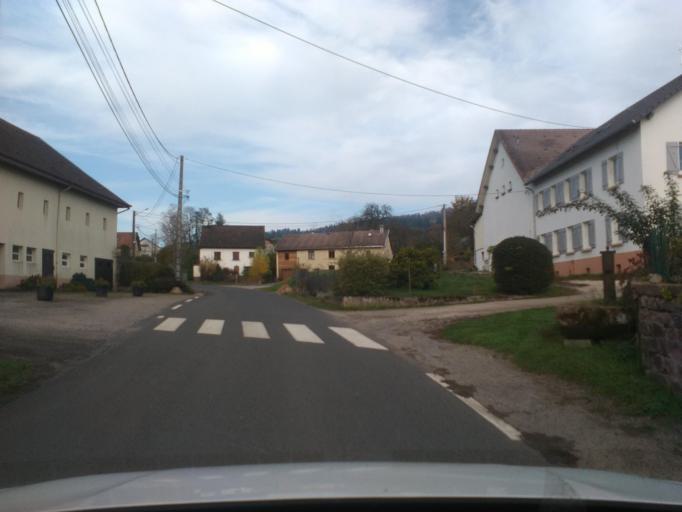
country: FR
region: Lorraine
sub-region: Departement des Vosges
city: Moyenmoutier
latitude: 48.3500
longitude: 6.9335
